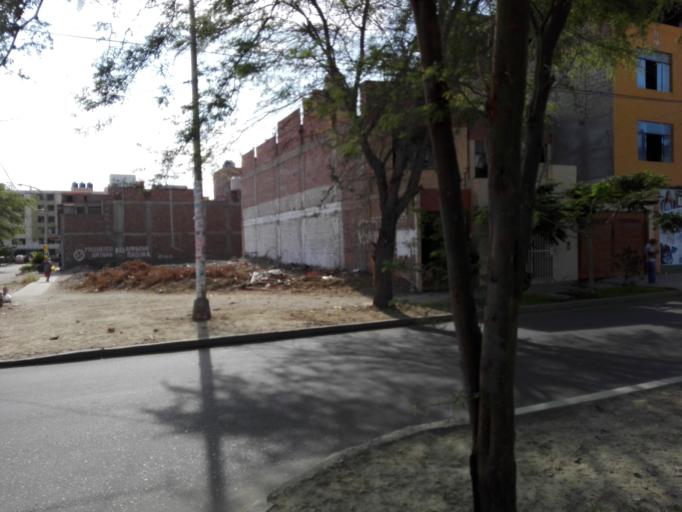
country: PE
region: Piura
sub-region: Provincia de Piura
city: Piura
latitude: -5.1858
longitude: -80.6178
